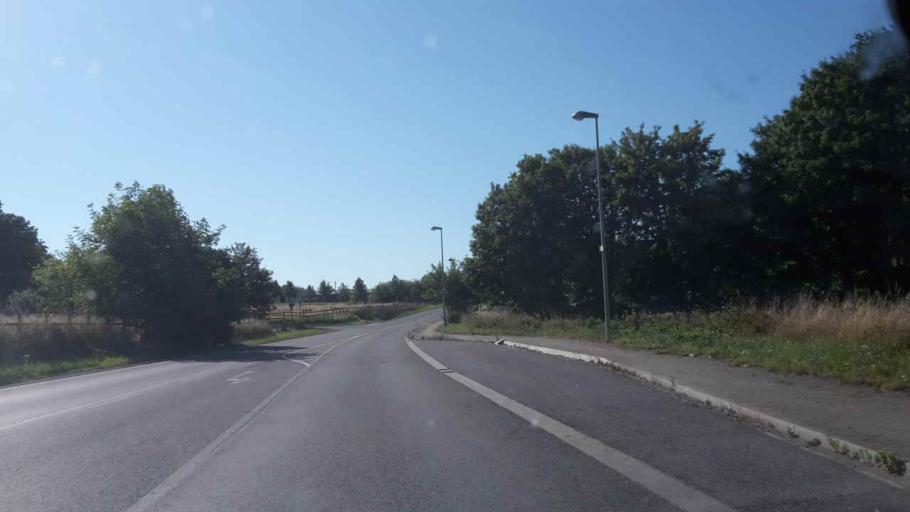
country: DE
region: North Rhine-Westphalia
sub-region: Regierungsbezirk Arnsberg
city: Hagen
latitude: 51.3712
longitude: 7.5361
